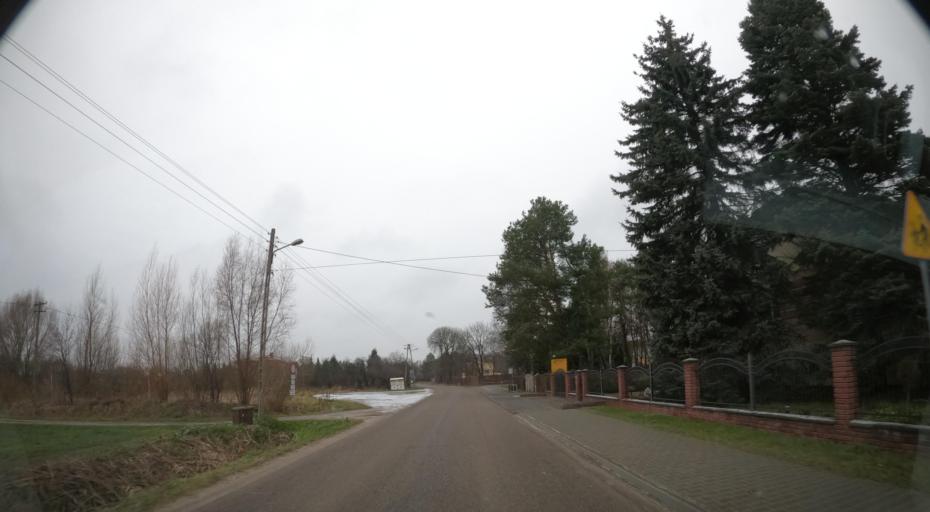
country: PL
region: Masovian Voivodeship
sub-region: Powiat radomski
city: Skaryszew
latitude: 51.3788
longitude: 21.2479
